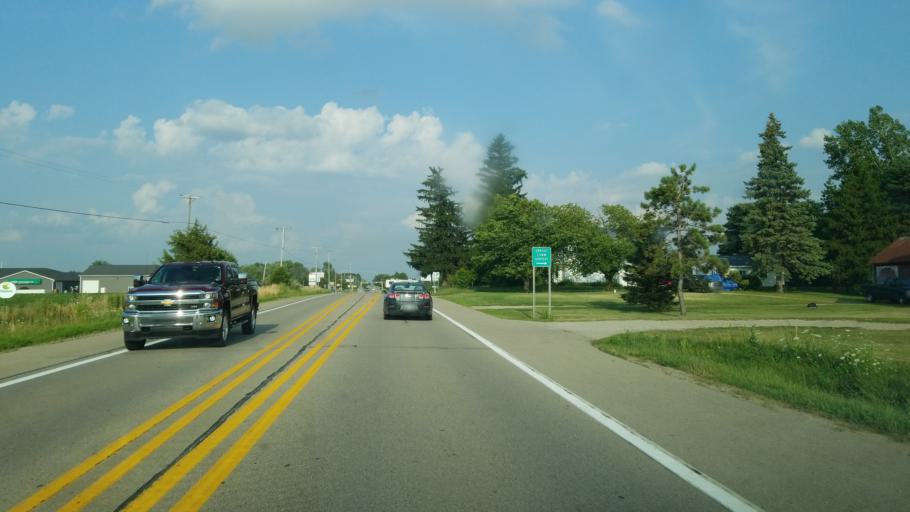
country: US
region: Michigan
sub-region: Gratiot County
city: Alma
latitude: 43.4080
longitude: -84.6891
